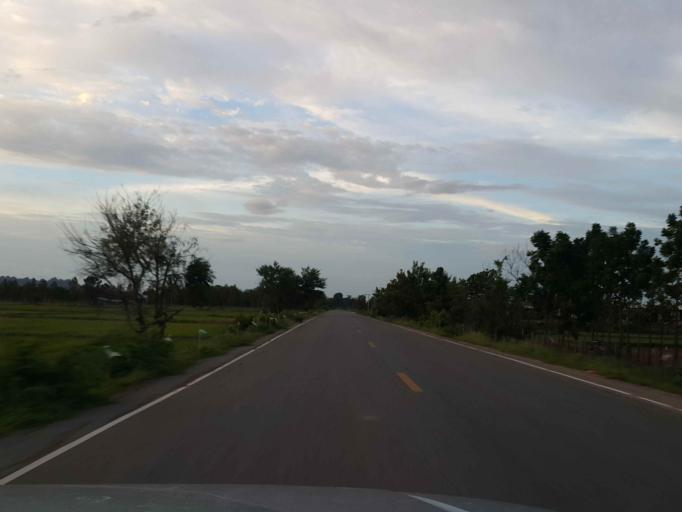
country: TH
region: Sukhothai
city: Ban Dan Lan Hoi
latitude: 17.0956
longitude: 99.5896
